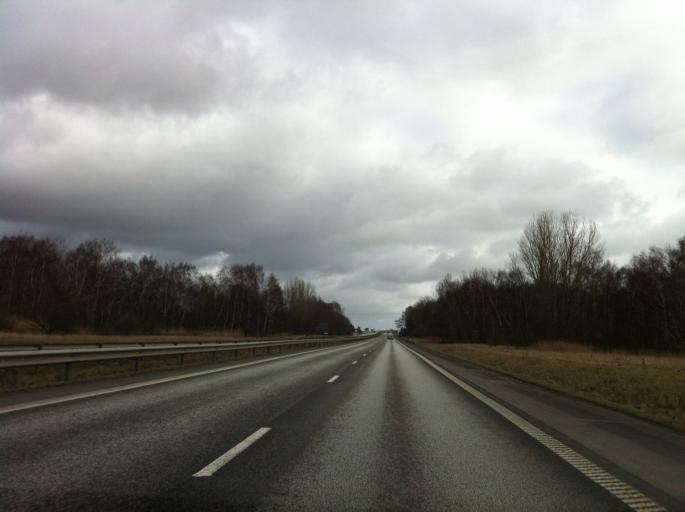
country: SE
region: Skane
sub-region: Kristianstads Kommun
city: Kristianstad
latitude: 56.0278
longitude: 14.0885
